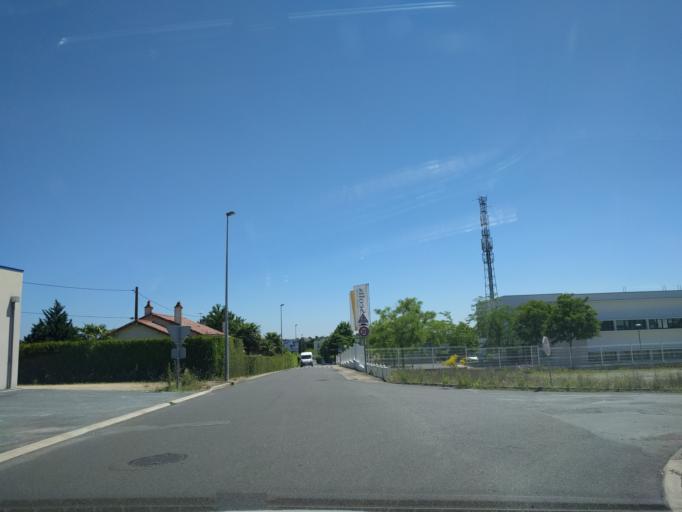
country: FR
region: Poitou-Charentes
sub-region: Departement des Deux-Sevres
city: Niort
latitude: 46.3366
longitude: -0.4206
